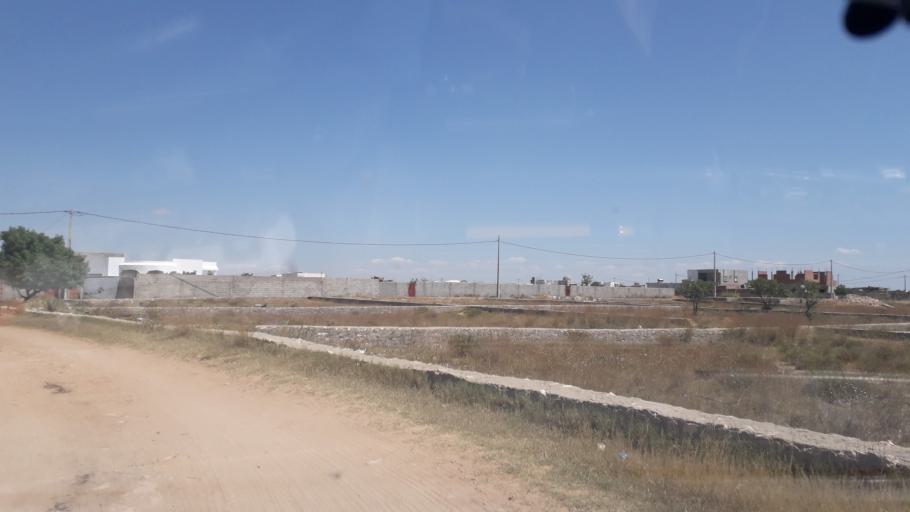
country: TN
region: Safaqis
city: Al Qarmadah
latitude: 34.8332
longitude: 10.7719
